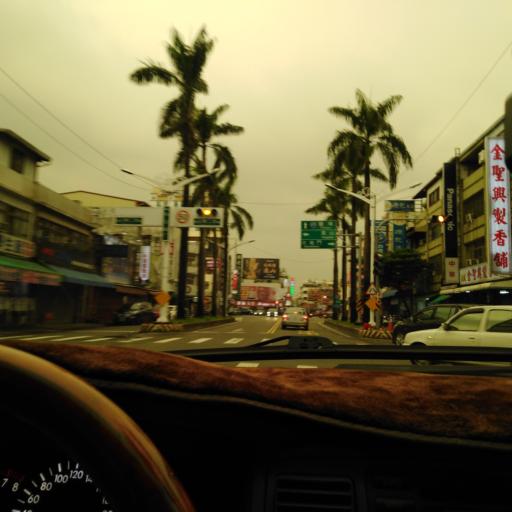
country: TW
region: Taiwan
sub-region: Pingtung
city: Pingtung
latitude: 22.6816
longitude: 120.4917
